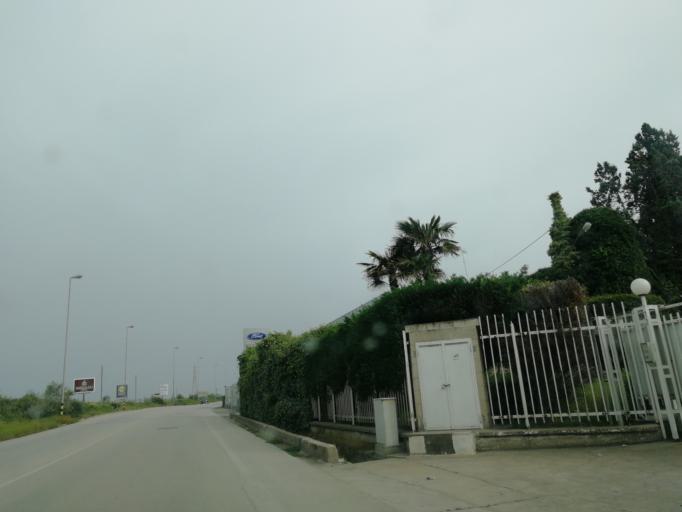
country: IT
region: Apulia
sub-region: Provincia di Barletta - Andria - Trani
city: Barletta
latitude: 41.3155
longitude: 16.2997
